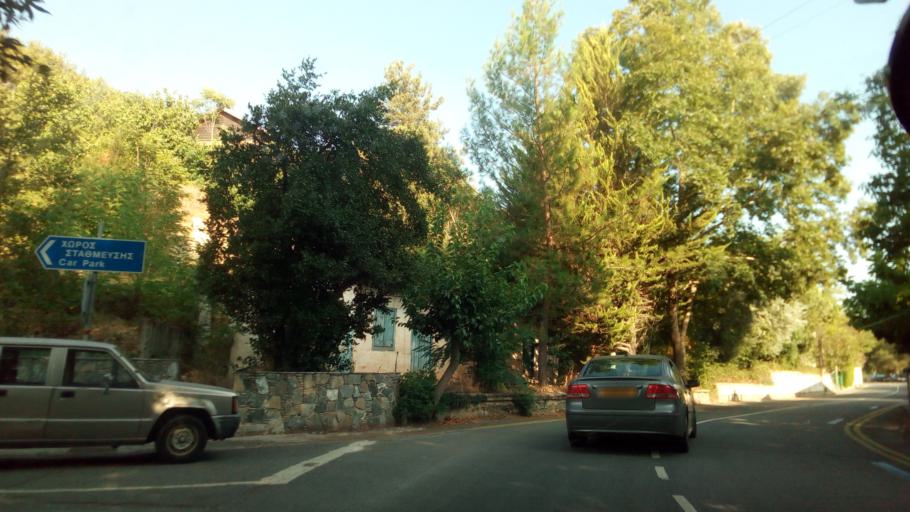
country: CY
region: Limassol
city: Pelendri
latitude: 34.8612
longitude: 32.8728
